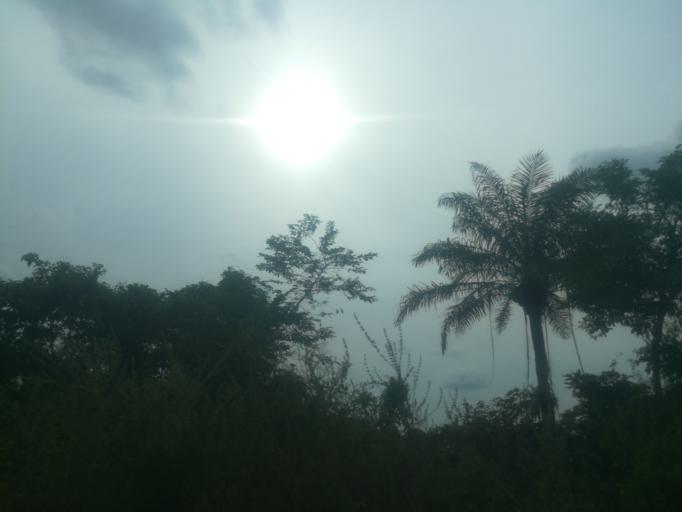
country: NG
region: Ogun
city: Ayetoro
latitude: 7.2948
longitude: 3.0782
